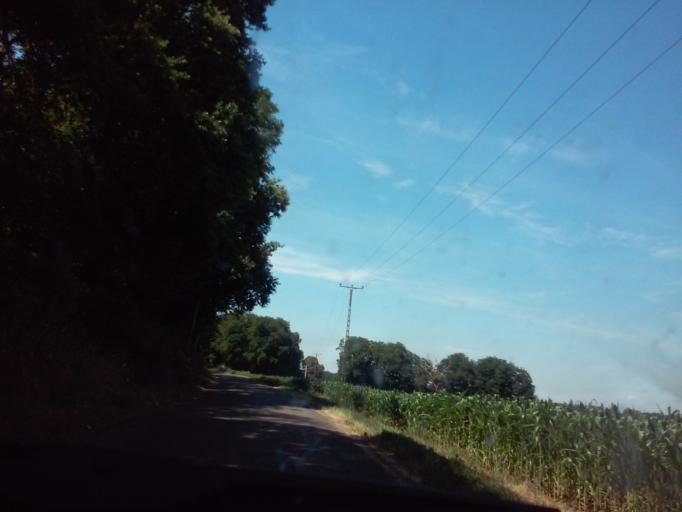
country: FR
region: Pays de la Loire
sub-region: Departement de la Sarthe
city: Beaufay
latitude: 48.1213
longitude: 0.3598
